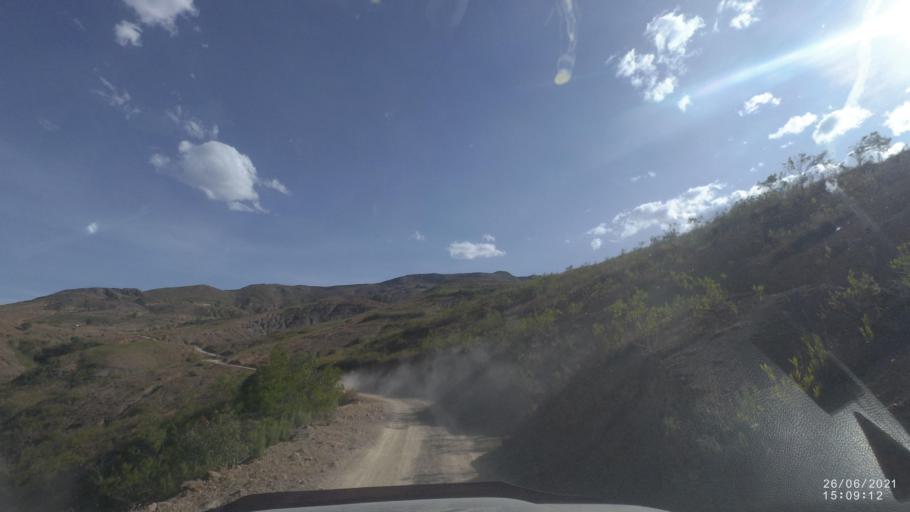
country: BO
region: Cochabamba
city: Mizque
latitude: -17.9508
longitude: -65.6393
